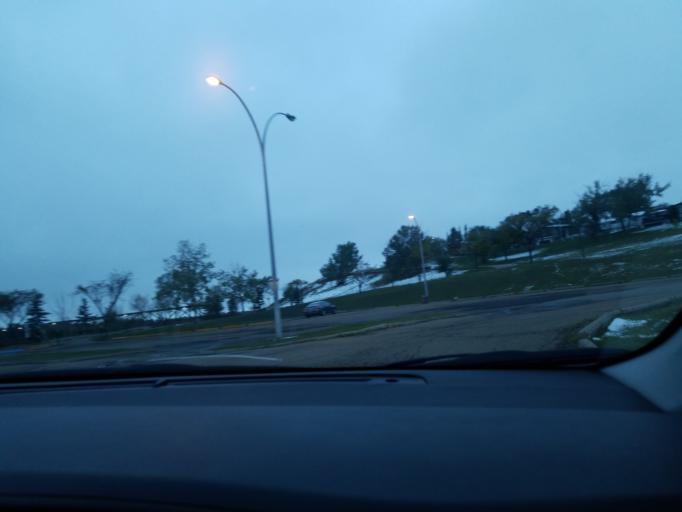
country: CA
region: Alberta
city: Edmonton
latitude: 53.5551
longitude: -113.3944
